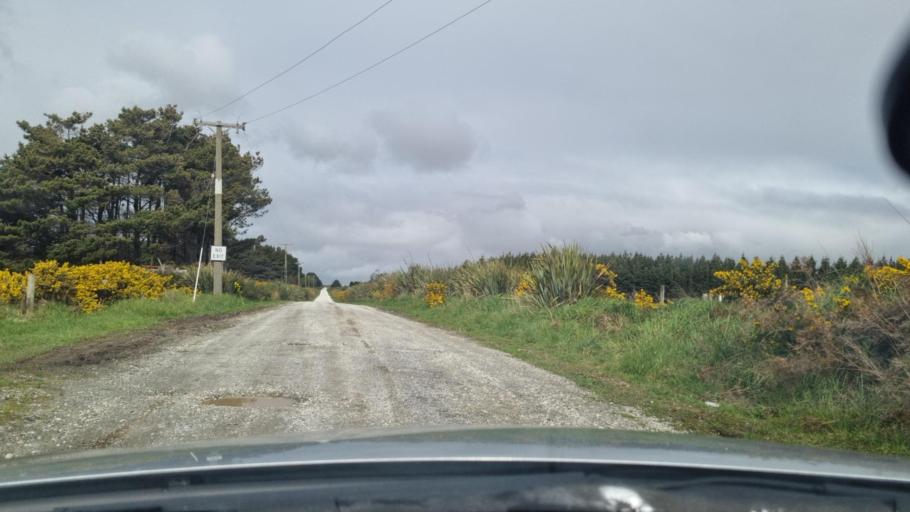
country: NZ
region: Southland
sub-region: Invercargill City
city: Bluff
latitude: -46.5105
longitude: 168.3502
